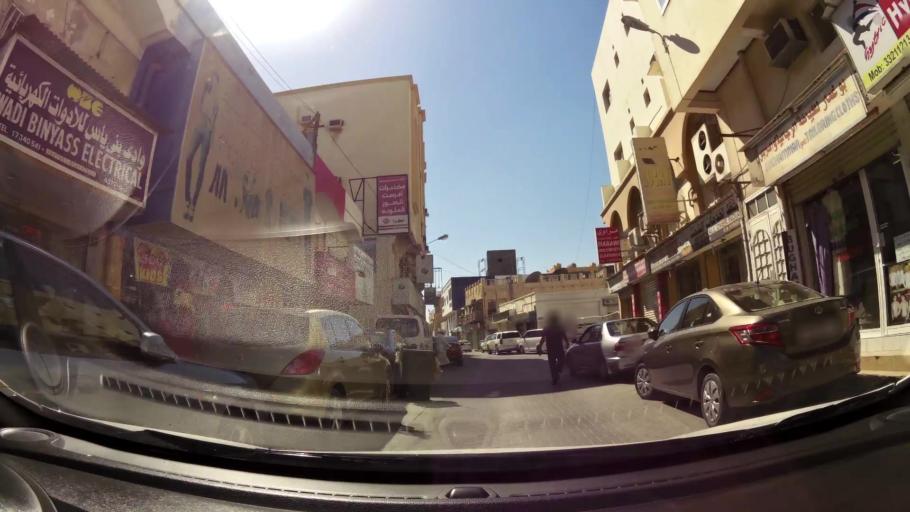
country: BH
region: Muharraq
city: Al Muharraq
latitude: 26.2494
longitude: 50.6101
